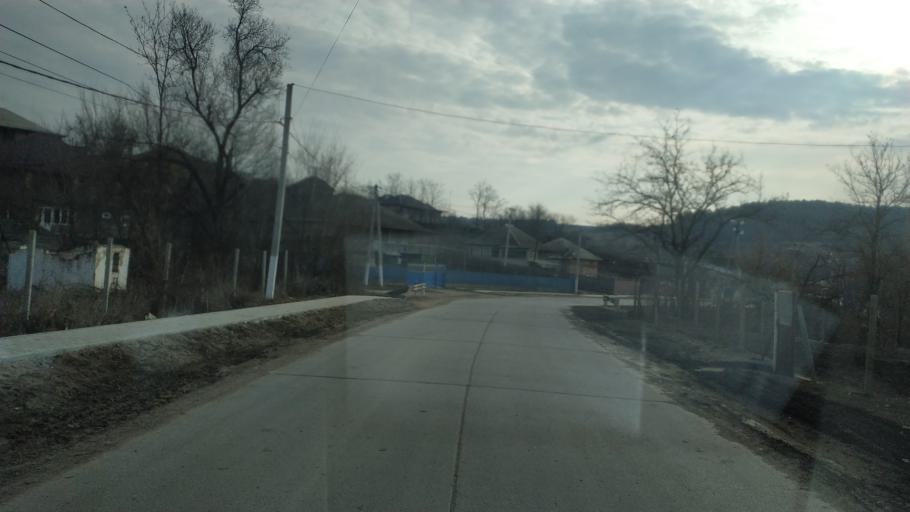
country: MD
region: Chisinau
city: Vadul lui Voda
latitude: 47.0076
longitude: 29.1205
